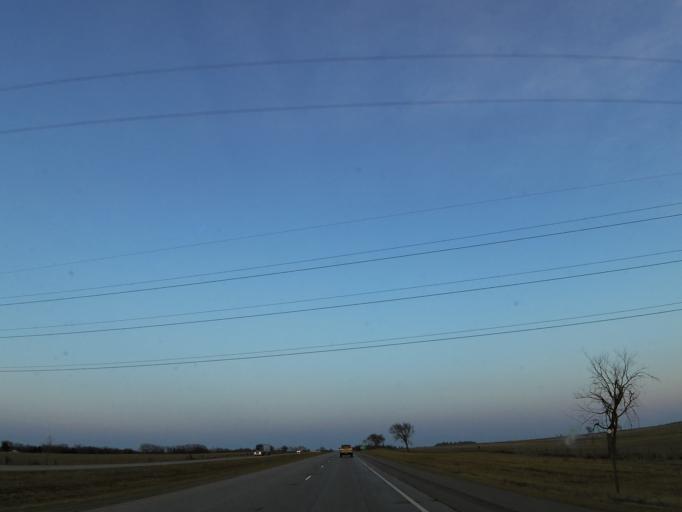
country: US
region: Minnesota
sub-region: Mower County
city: Austin
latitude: 43.6713
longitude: -92.8995
